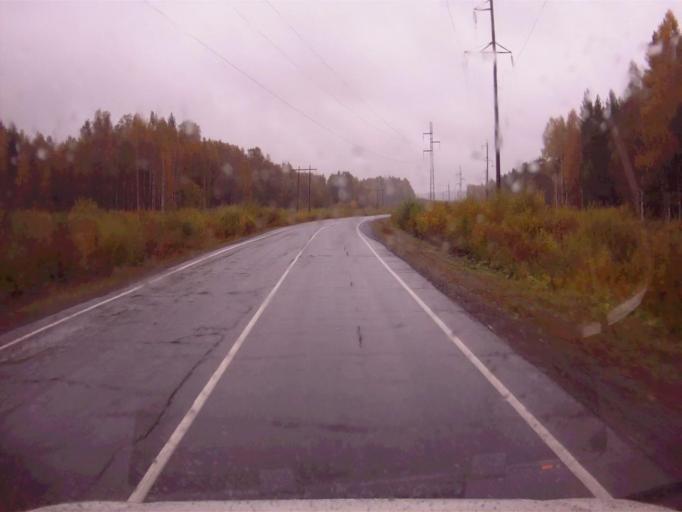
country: RU
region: Chelyabinsk
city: Verkhniy Ufaley
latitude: 55.9451
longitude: 60.4059
